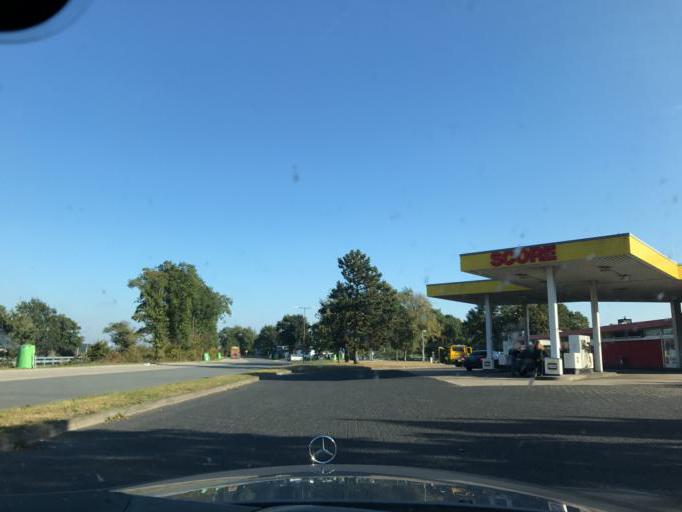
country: DE
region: Lower Saxony
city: Ganderkesee
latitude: 53.0549
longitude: 8.5002
